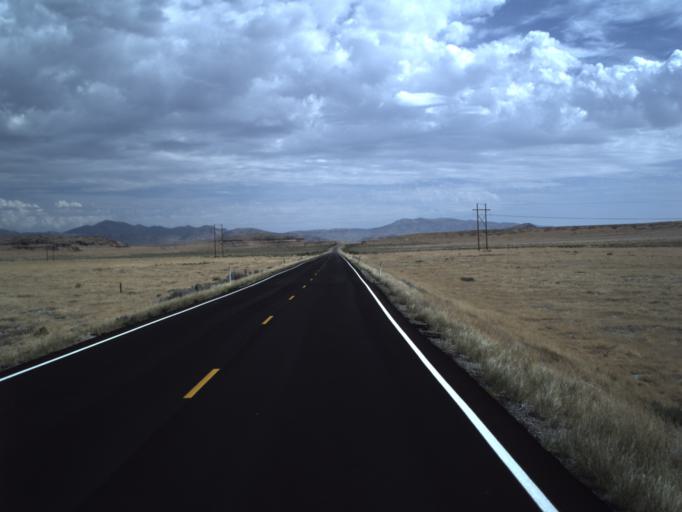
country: US
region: Utah
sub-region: Tooele County
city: Wendover
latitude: 41.4117
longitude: -113.9264
